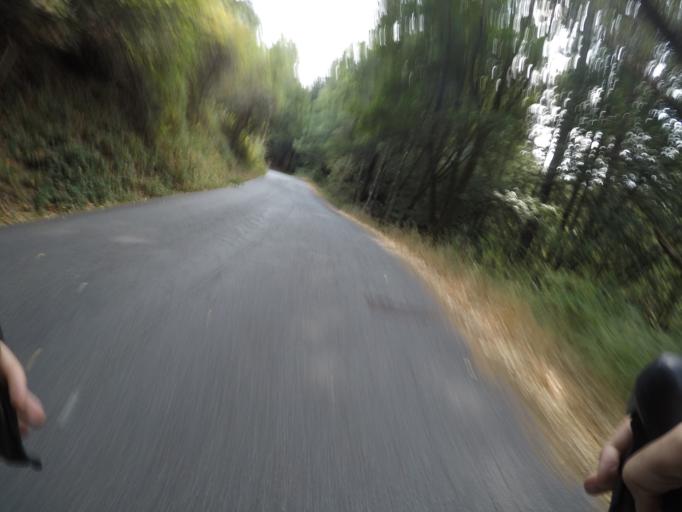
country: US
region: California
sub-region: Santa Cruz County
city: Scotts Valley
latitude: 37.0844
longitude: -122.0098
